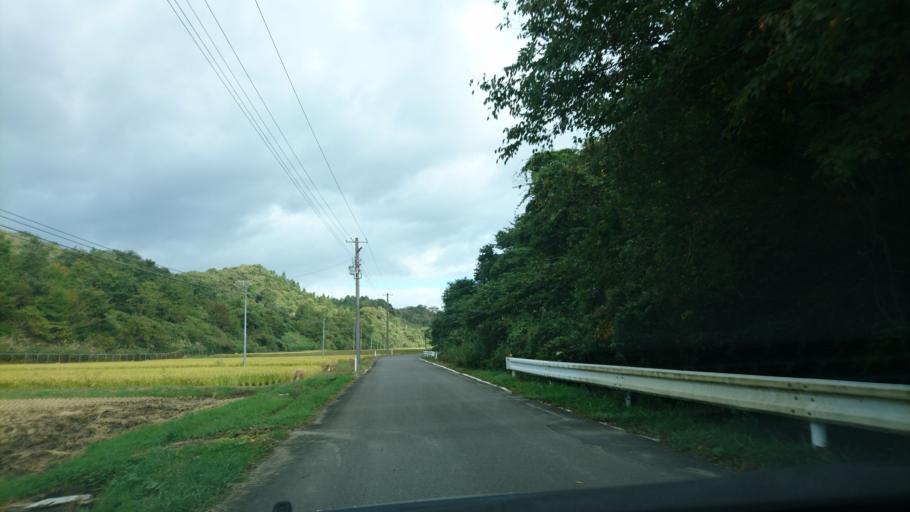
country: JP
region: Iwate
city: Ichinoseki
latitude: 38.8756
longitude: 141.0939
